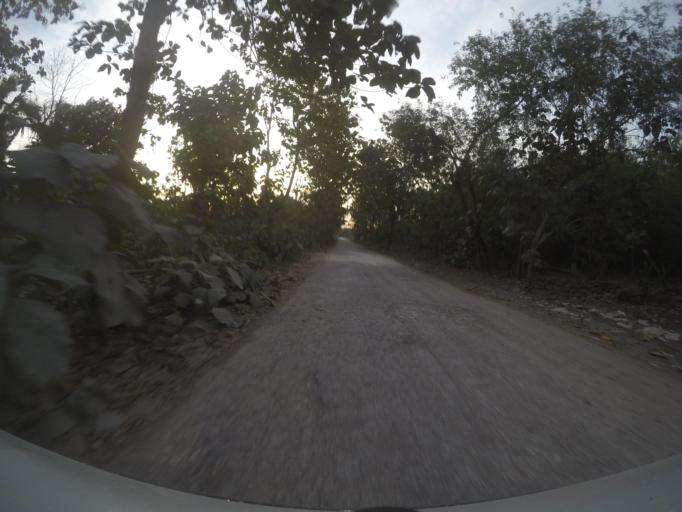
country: TL
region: Viqueque
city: Viqueque
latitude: -8.9407
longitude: 126.4218
